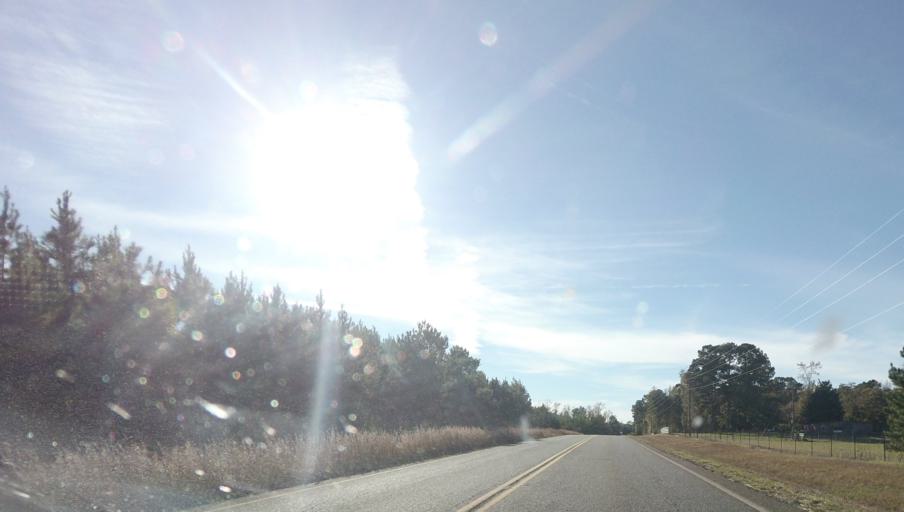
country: US
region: Georgia
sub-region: Talbot County
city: Talbotton
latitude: 32.6809
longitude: -84.6486
